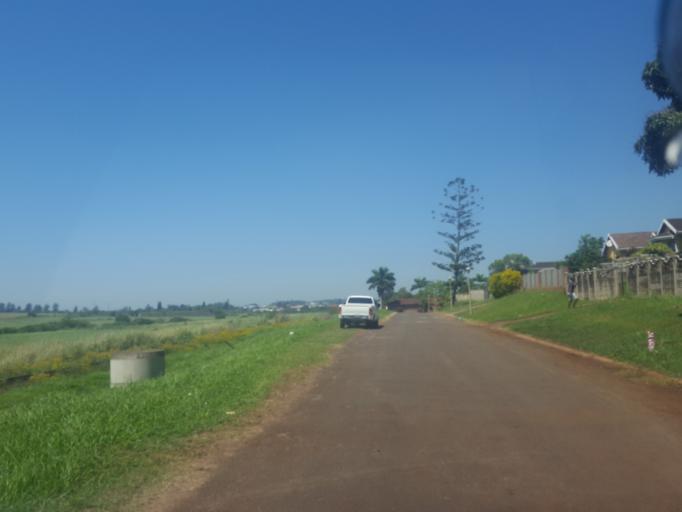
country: ZA
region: KwaZulu-Natal
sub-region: uThungulu District Municipality
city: Empangeni
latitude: -28.7518
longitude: 31.9087
